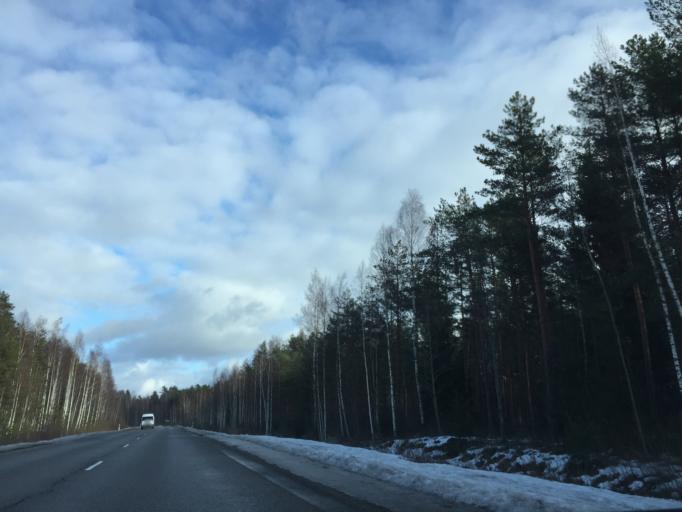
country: LV
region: Salacgrivas
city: Ainazi
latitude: 57.8566
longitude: 24.5278
